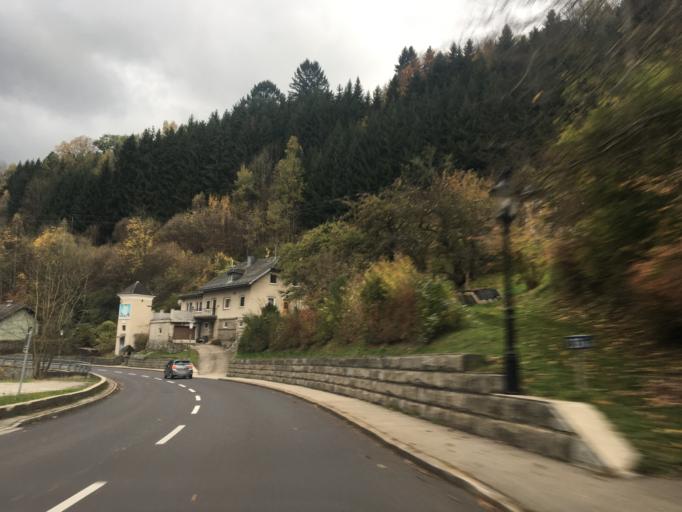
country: AT
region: Upper Austria
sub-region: Politischer Bezirk Urfahr-Umgebung
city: Herzogsdorf
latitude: 48.5425
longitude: 14.1399
